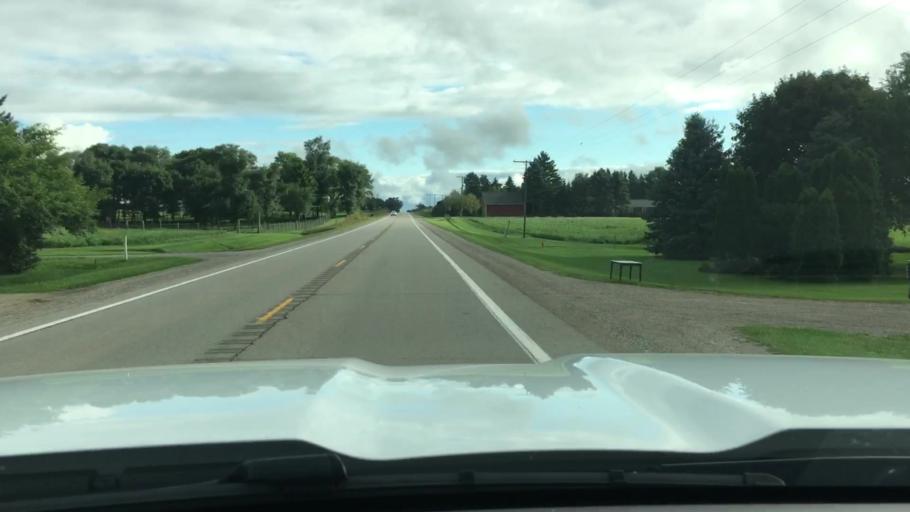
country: US
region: Michigan
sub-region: Tuscola County
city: Caro
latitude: 43.5440
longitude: -83.3340
